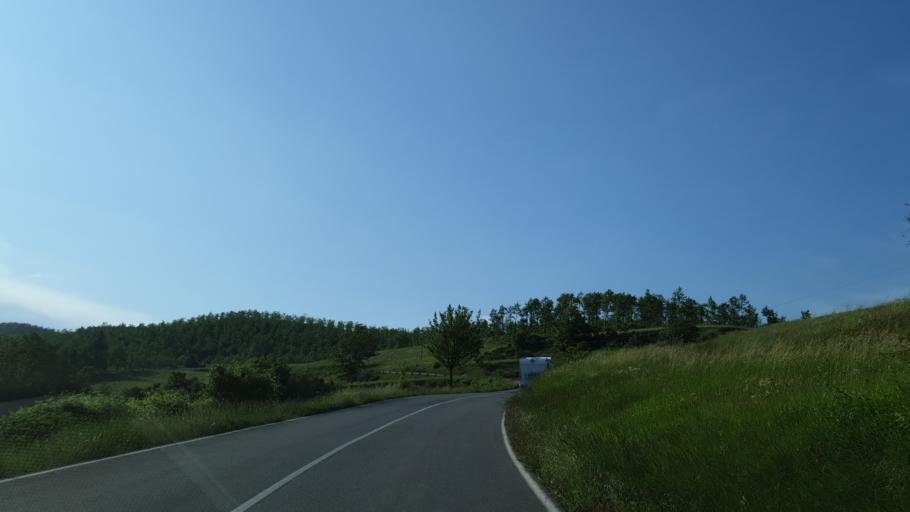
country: IT
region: Tuscany
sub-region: Province of Arezzo
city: Stia
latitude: 43.7756
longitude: 11.6858
